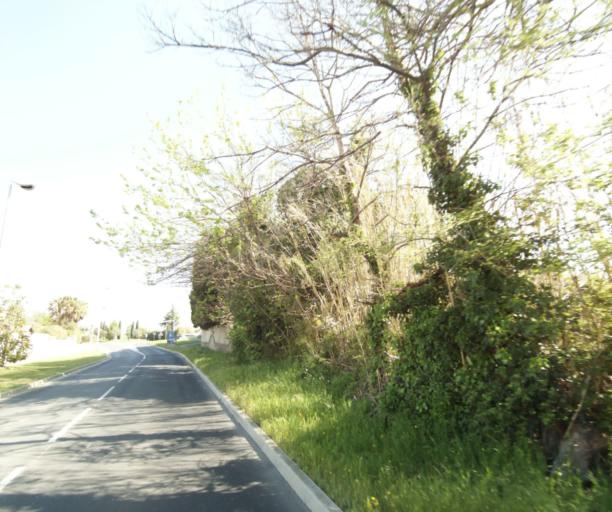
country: FR
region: Languedoc-Roussillon
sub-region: Departement de l'Herault
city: Lattes
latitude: 43.5770
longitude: 3.9074
